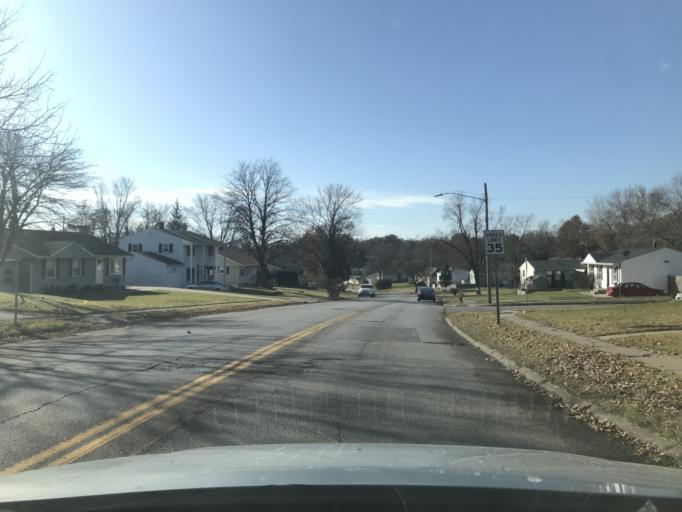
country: US
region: Iowa
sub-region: Scott County
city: Davenport
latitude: 41.5308
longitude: -90.6137
